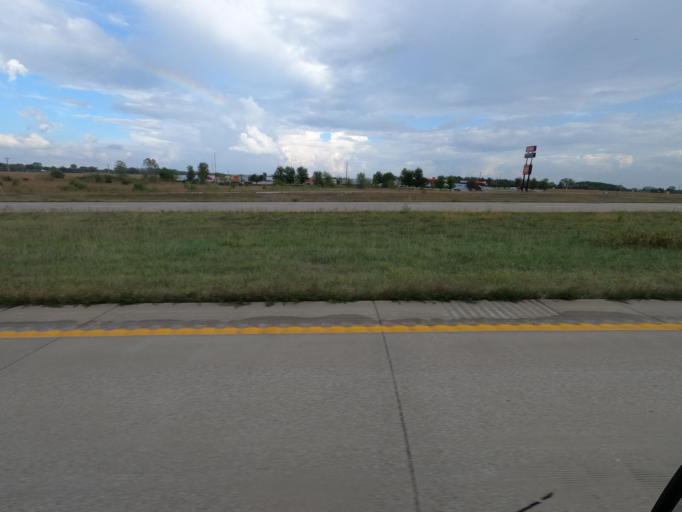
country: US
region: Illinois
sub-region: Hancock County
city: Warsaw
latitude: 40.3965
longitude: -91.5728
